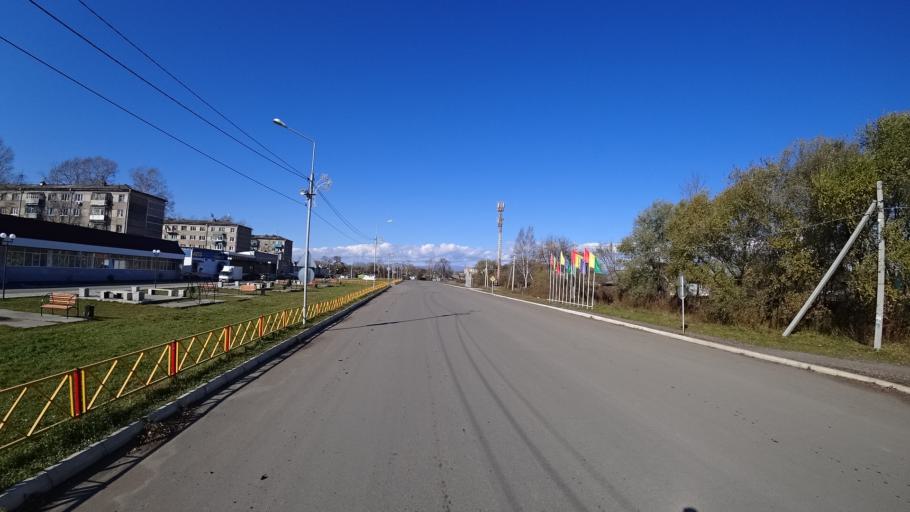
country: RU
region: Khabarovsk Krai
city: Amursk
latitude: 50.1003
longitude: 136.5126
